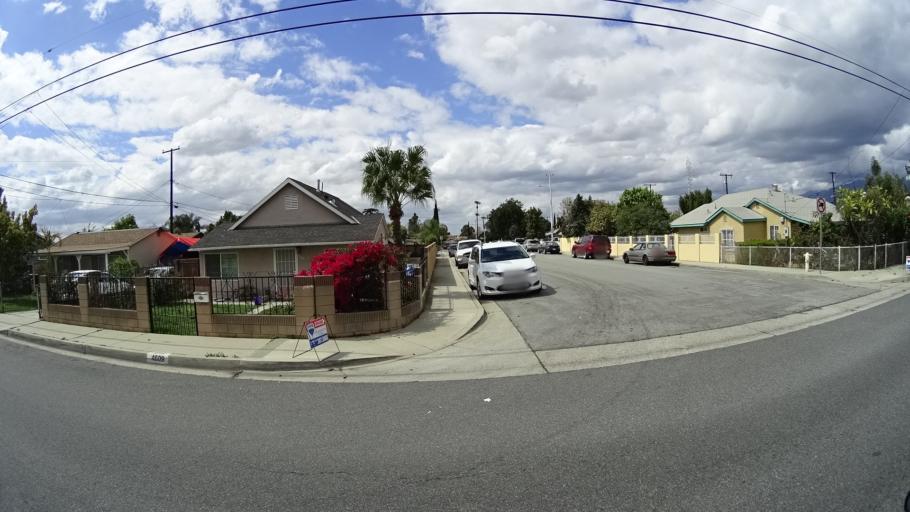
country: US
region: California
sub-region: Los Angeles County
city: Baldwin Park
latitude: 34.0959
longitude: -117.9780
